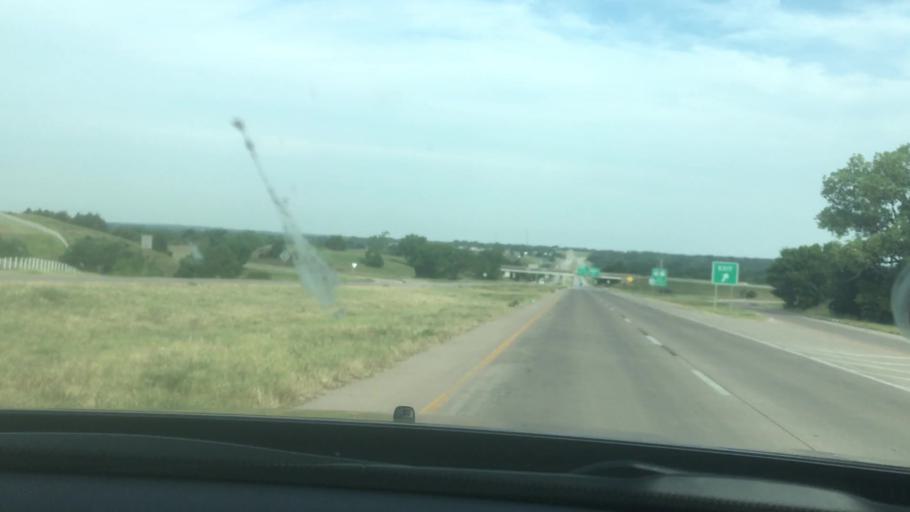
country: US
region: Oklahoma
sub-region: Pontotoc County
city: Ada
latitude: 34.7747
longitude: -96.6979
